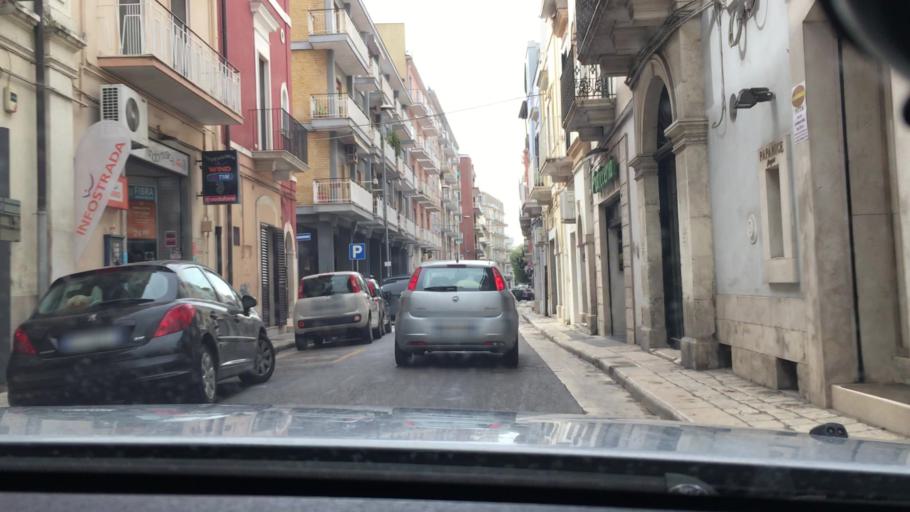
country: IT
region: Apulia
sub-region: Provincia di Bari
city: Gioia del Colle
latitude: 40.7974
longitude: 16.9205
